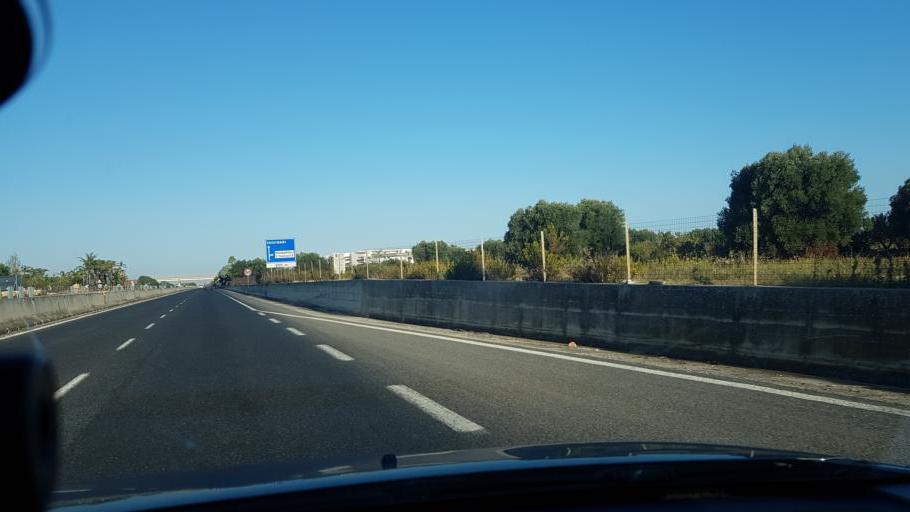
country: IT
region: Apulia
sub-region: Provincia di Bari
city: Monopoli
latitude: 40.9282
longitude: 17.3067
